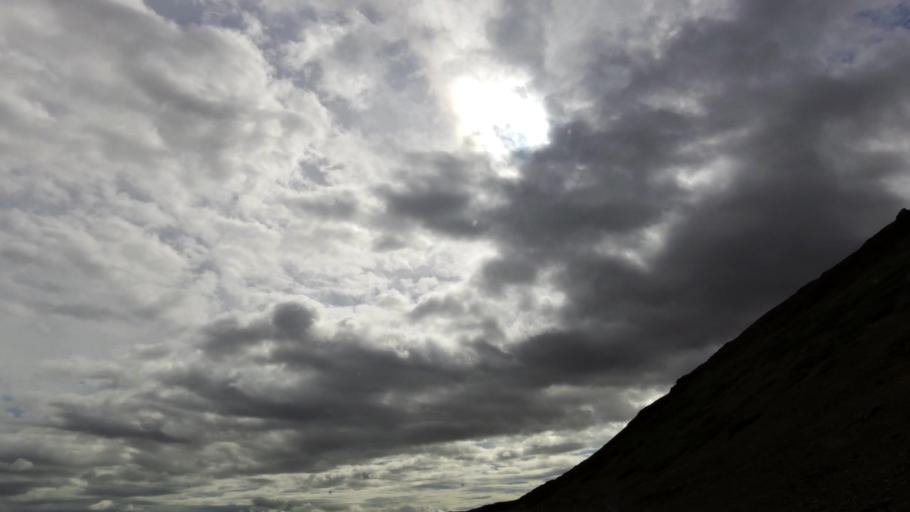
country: IS
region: West
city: Stykkisholmur
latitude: 65.5975
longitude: -22.1201
